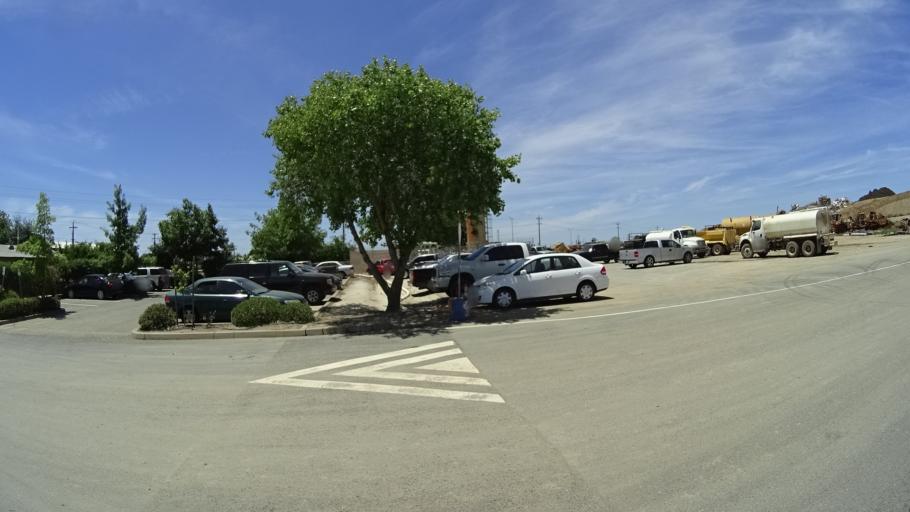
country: US
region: California
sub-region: Sacramento County
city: Rosemont
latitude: 38.5258
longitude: -121.3848
